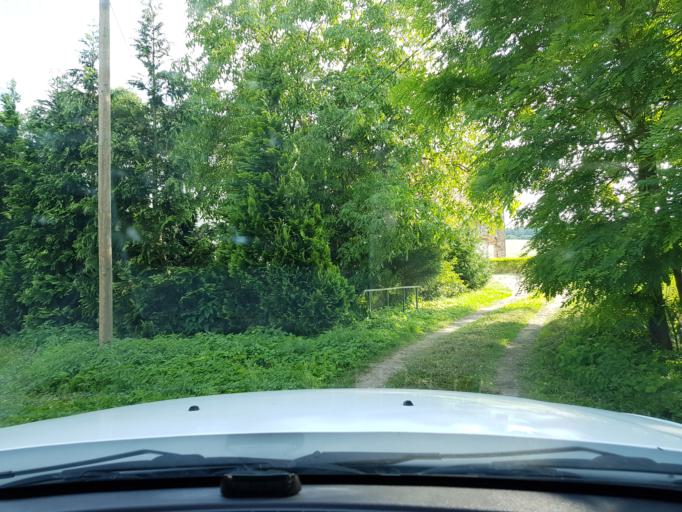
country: PL
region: West Pomeranian Voivodeship
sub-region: Powiat gryfinski
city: Chojna
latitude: 52.9968
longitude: 14.4828
